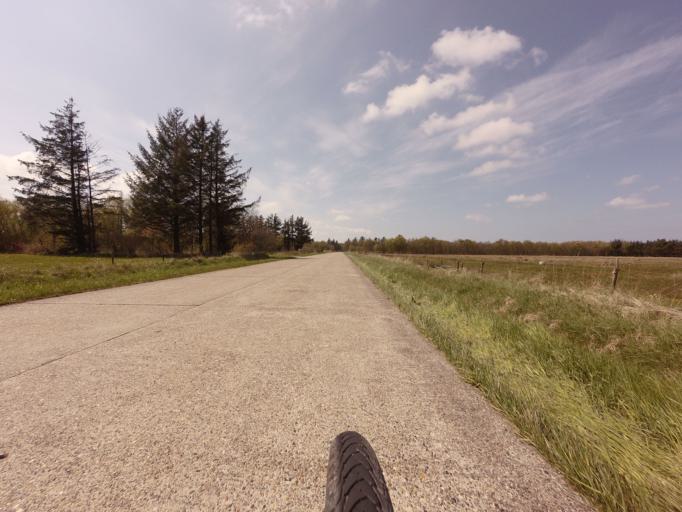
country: DK
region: North Denmark
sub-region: Jammerbugt Kommune
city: Brovst
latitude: 57.1644
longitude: 9.4920
